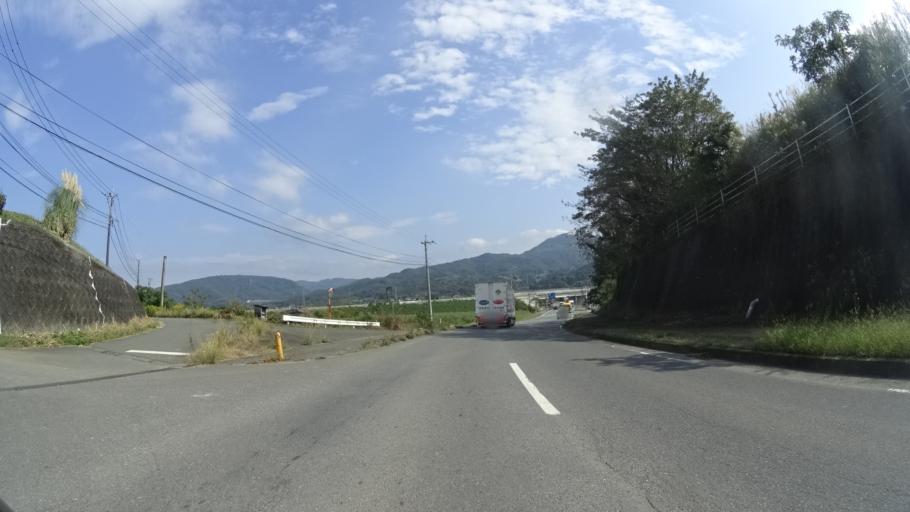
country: JP
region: Kumamoto
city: Kumamoto
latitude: 32.7494
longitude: 130.7971
